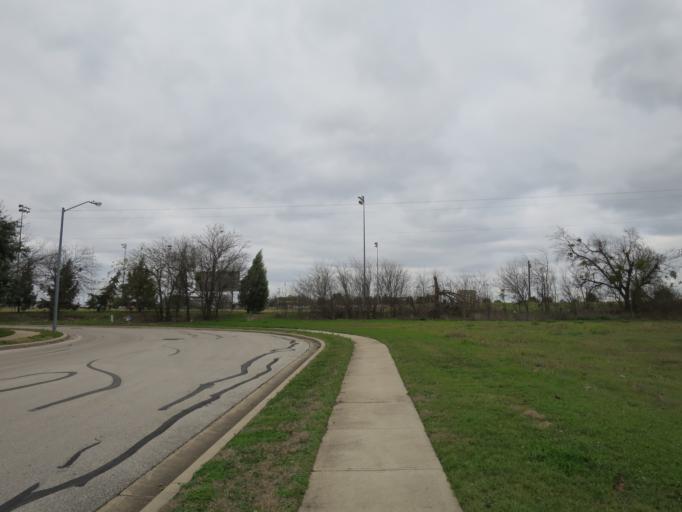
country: US
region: Texas
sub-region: Williamson County
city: Round Rock
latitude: 30.5397
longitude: -97.6227
